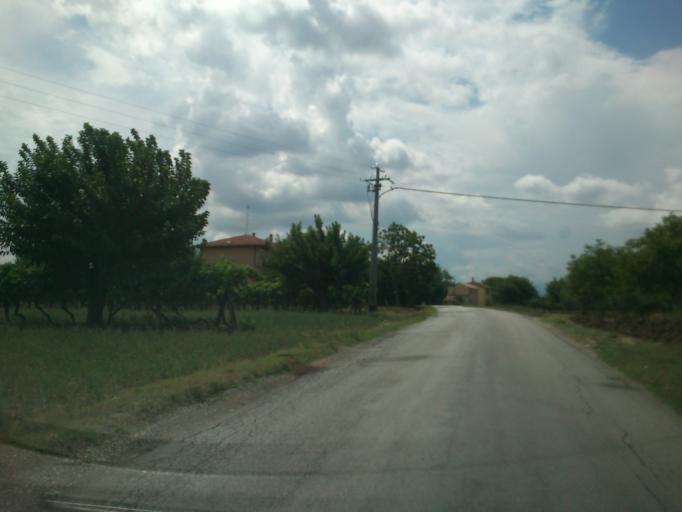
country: IT
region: The Marches
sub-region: Provincia di Pesaro e Urbino
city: Villanova
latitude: 43.7393
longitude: 12.9294
